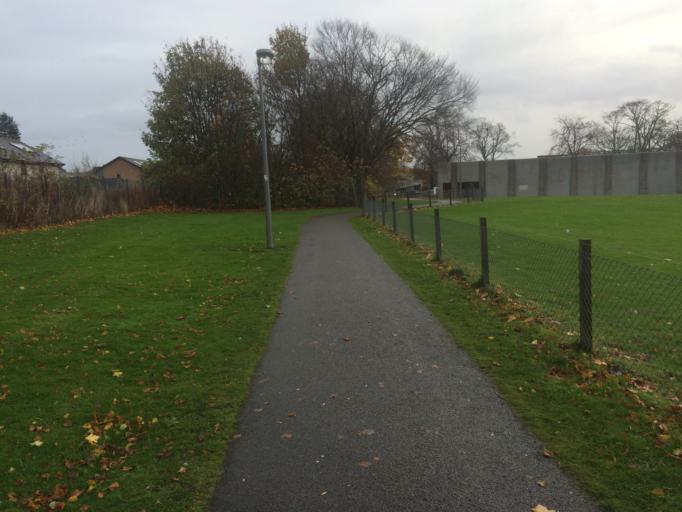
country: GB
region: Scotland
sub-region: Highland
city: Alness
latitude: 57.6946
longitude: -4.2530
